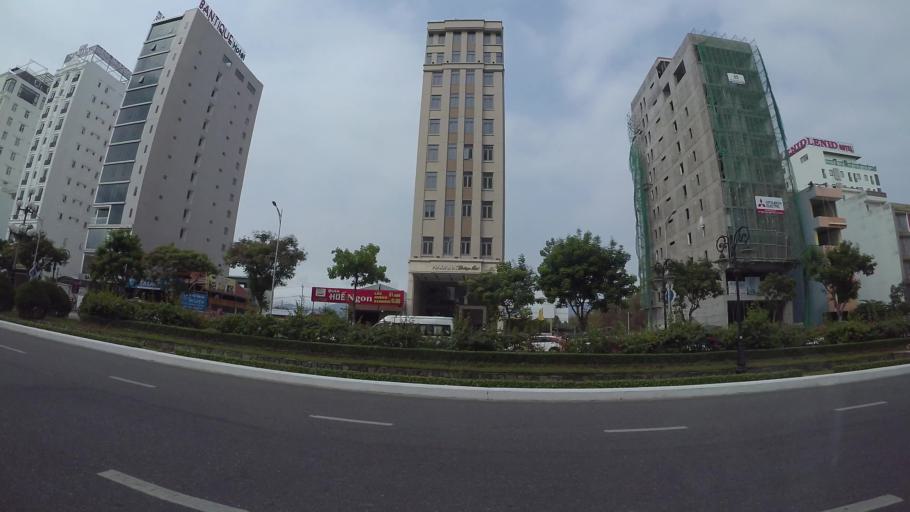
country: VN
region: Da Nang
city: Son Tra
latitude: 16.0711
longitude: 108.2353
